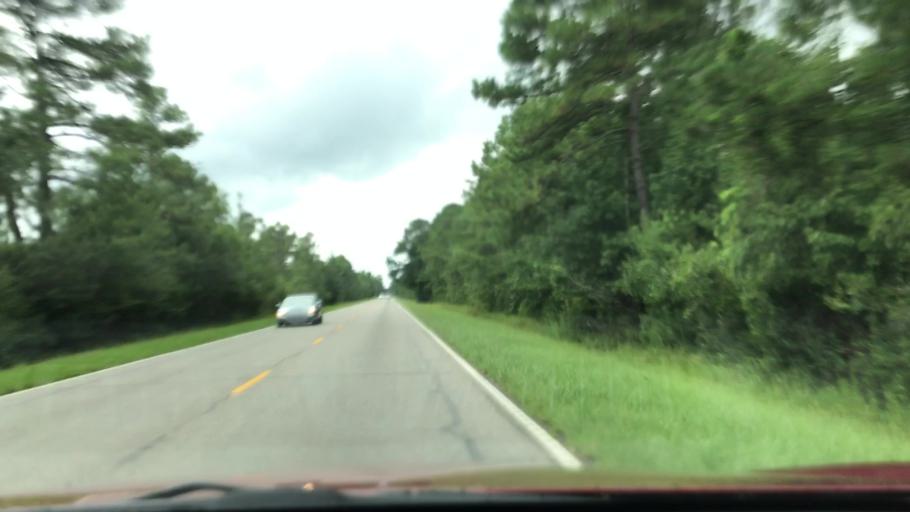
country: US
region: South Carolina
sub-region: Georgetown County
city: Georgetown
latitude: 33.5407
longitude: -79.2294
